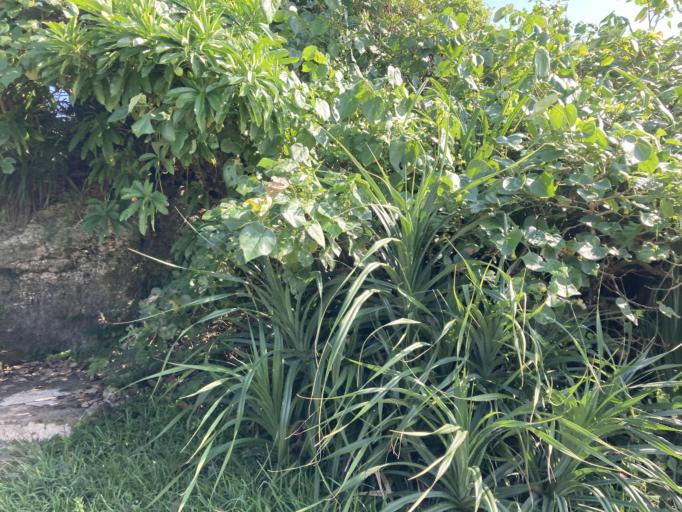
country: JP
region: Okinawa
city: Chatan
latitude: 26.3637
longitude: 127.7377
